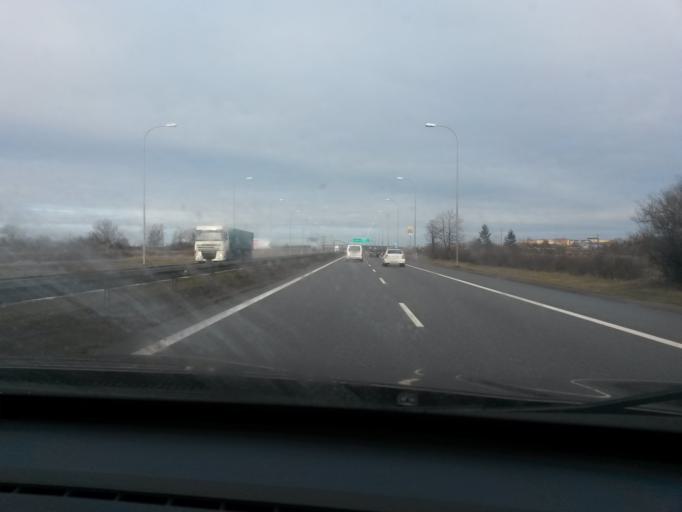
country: PL
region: Pomeranian Voivodeship
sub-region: Powiat nowodworski
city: Nowy Dwor Gdanski
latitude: 54.2055
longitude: 19.1094
